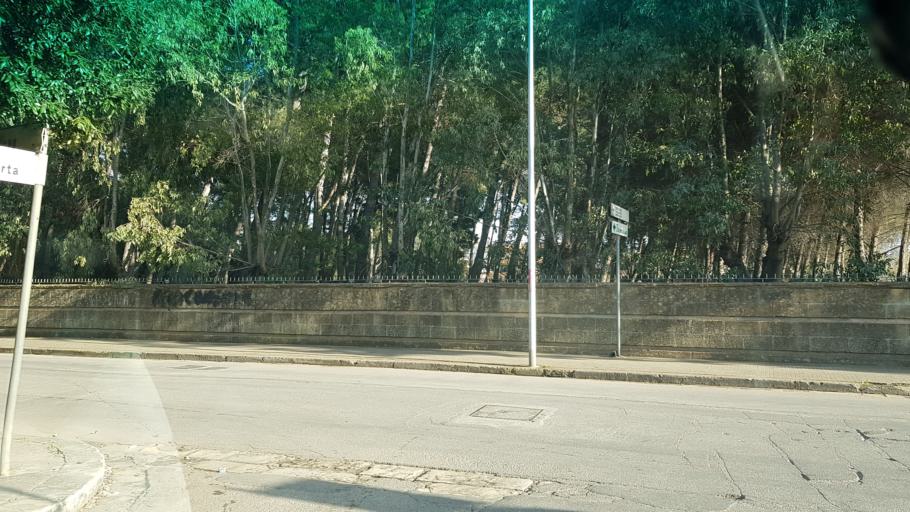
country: IT
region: Apulia
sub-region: Provincia di Brindisi
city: San Vito dei Normanni
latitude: 40.6617
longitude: 17.6987
